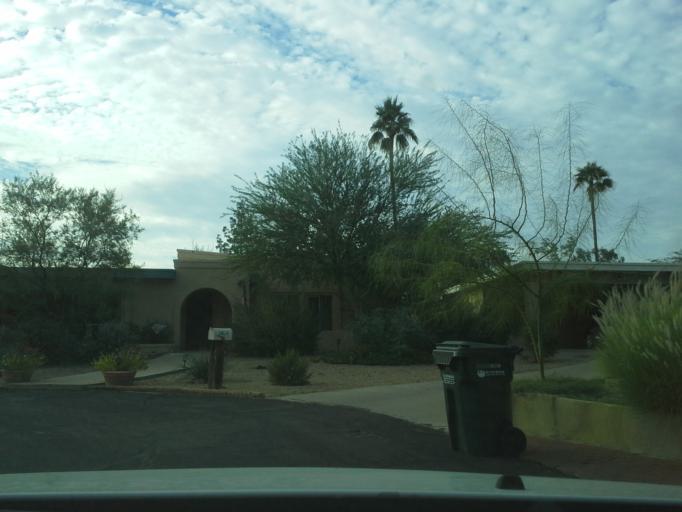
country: US
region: Arizona
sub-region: Maricopa County
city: Paradise Valley
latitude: 33.6103
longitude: -112.0590
